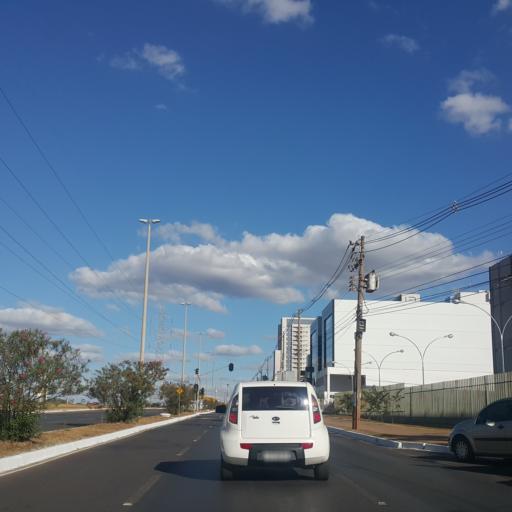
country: BR
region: Federal District
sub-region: Brasilia
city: Brasilia
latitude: -15.8352
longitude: -48.0456
